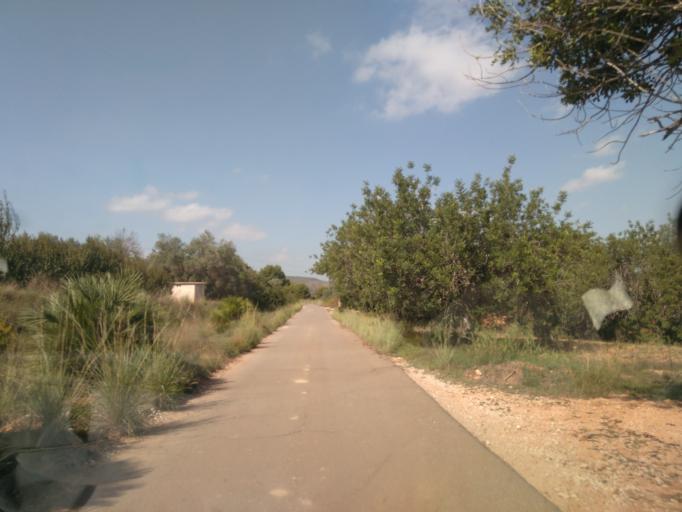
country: ES
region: Valencia
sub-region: Provincia de Valencia
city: Tous
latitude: 39.1739
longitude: -0.5930
